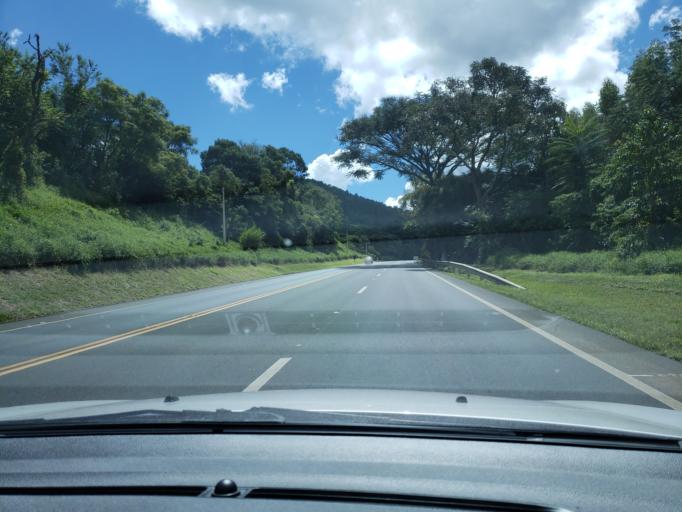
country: BR
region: Minas Gerais
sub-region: Pocos De Caldas
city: Pocos de Caldas
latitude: -21.8548
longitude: -46.6855
